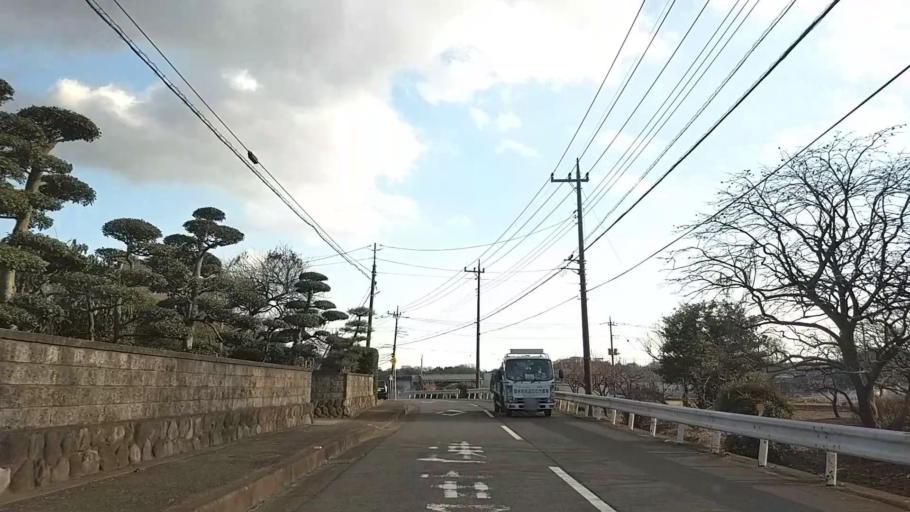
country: JP
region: Kanagawa
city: Atsugi
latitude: 35.4446
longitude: 139.3362
